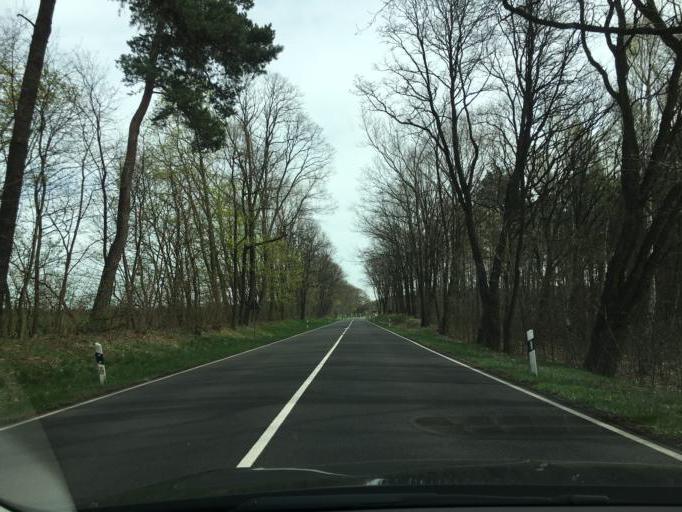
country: DE
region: Saxony
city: Gross Duben
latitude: 51.5756
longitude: 14.5291
